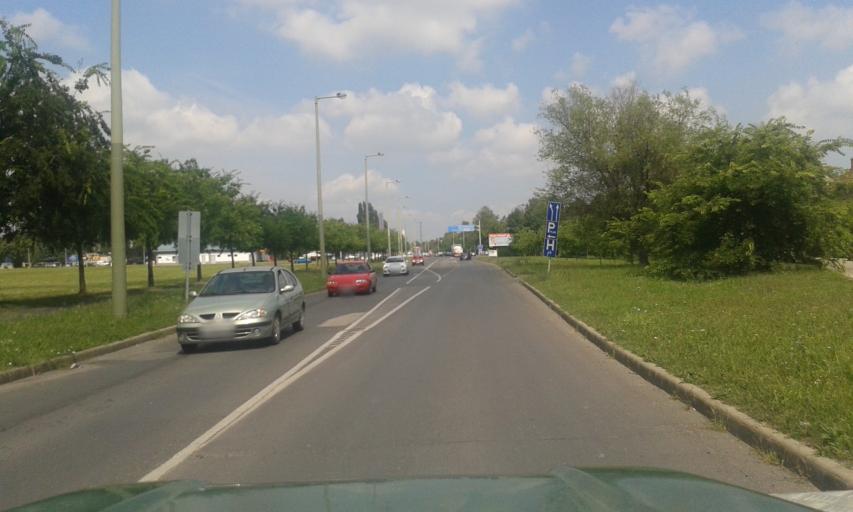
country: HU
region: Csongrad
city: Szeged
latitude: 46.2507
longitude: 20.1226
